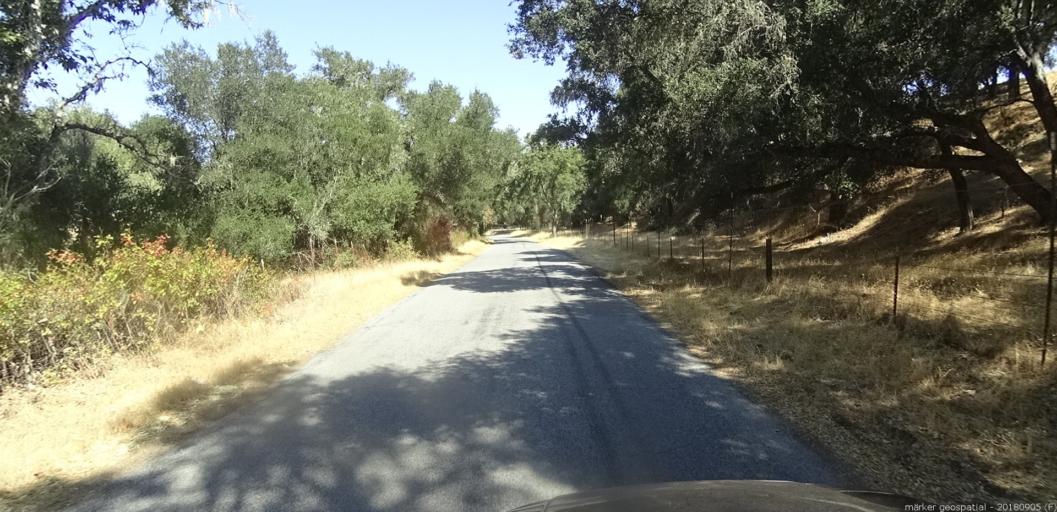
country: US
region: California
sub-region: Monterey County
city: Carmel Valley Village
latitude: 36.3973
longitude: -121.6507
